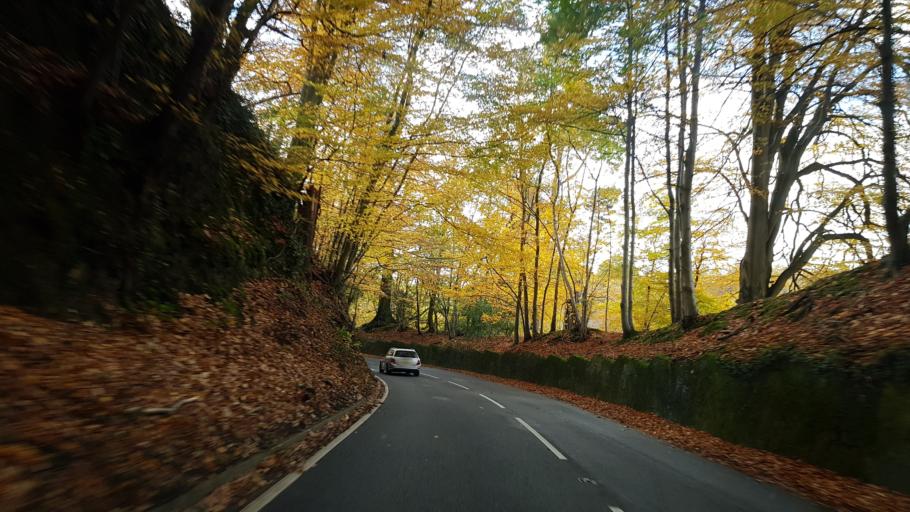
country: GB
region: England
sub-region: Surrey
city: Milford
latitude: 51.1393
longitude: -0.6723
